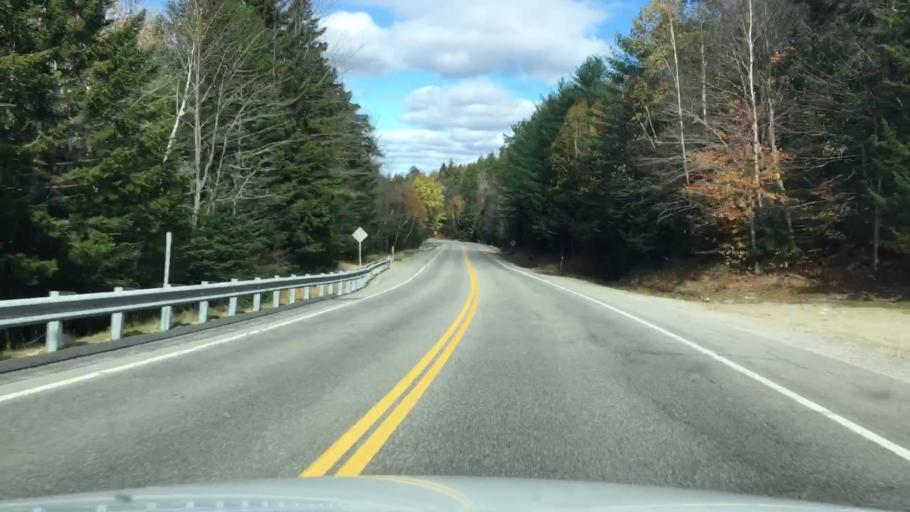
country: US
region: New Hampshire
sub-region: Coos County
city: Gorham
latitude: 44.3025
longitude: -71.2210
